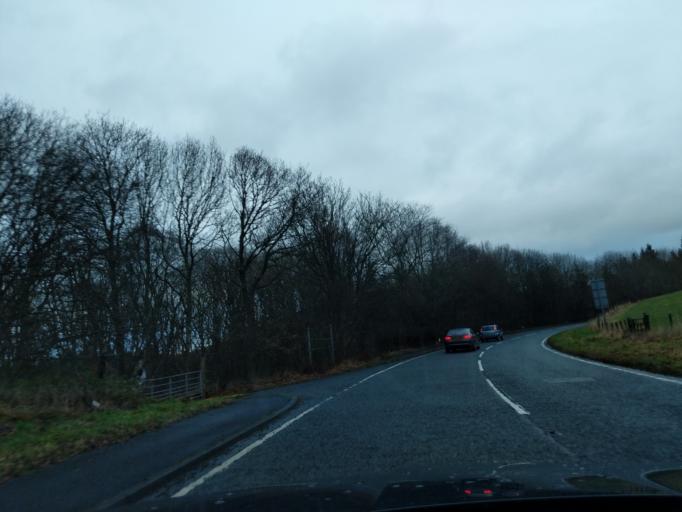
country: GB
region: Scotland
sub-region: The Scottish Borders
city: Galashiels
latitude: 55.6309
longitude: -2.8332
